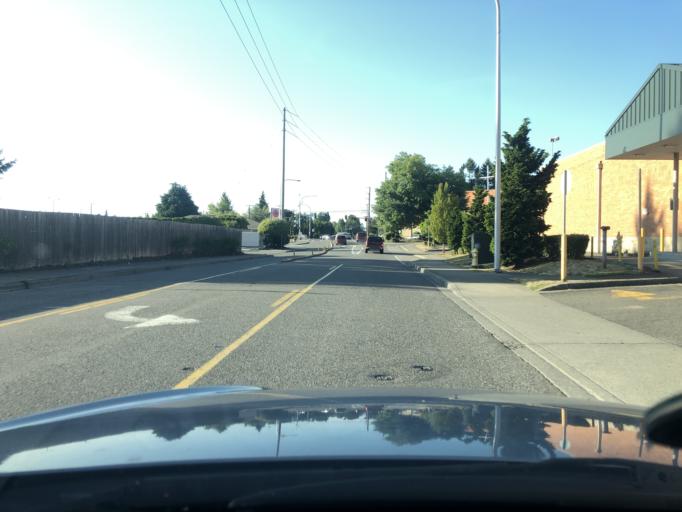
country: US
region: Washington
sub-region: King County
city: Auburn
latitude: 47.2927
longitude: -122.2133
